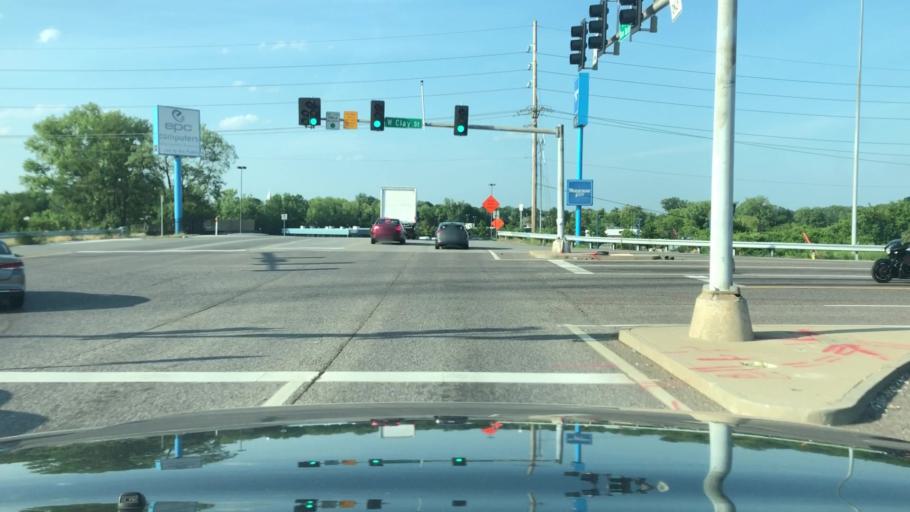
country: US
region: Missouri
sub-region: Saint Charles County
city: Saint Peters
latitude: 38.7948
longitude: -90.5643
